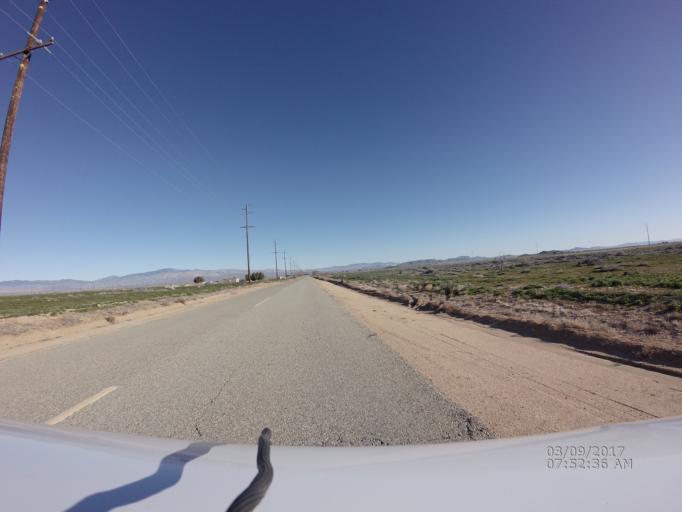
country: US
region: California
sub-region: Los Angeles County
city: Leona Valley
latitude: 34.7799
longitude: -118.3257
